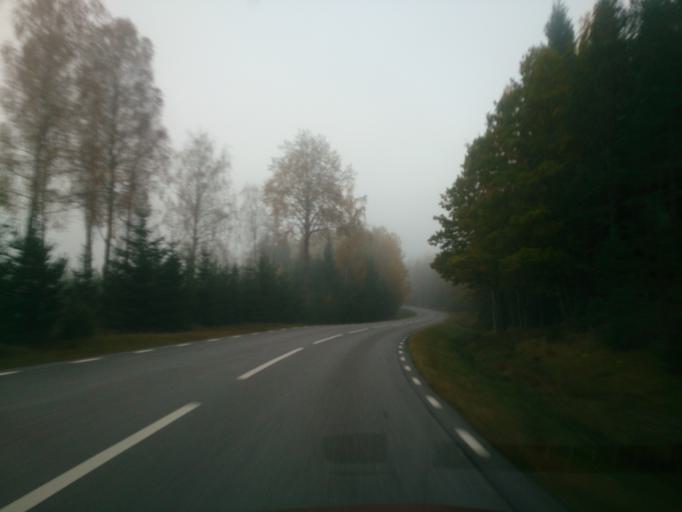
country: SE
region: OEstergoetland
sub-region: Atvidabergs Kommun
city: Atvidaberg
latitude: 58.1339
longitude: 15.9564
